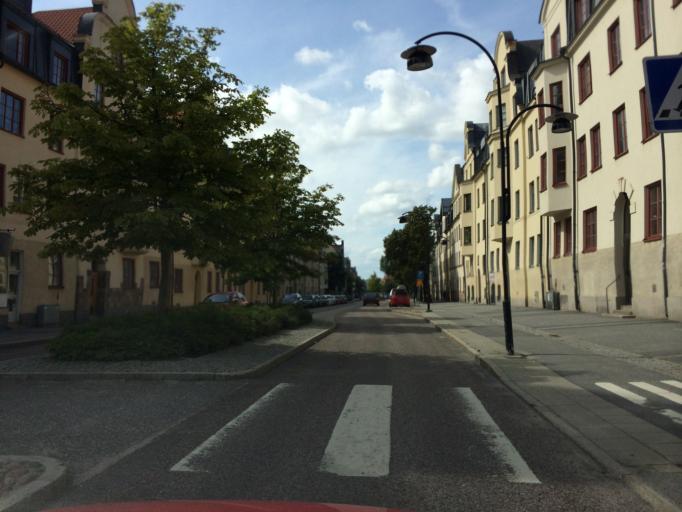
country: SE
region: Stockholm
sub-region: Stockholms Kommun
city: Arsta
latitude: 59.3057
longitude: 18.0067
